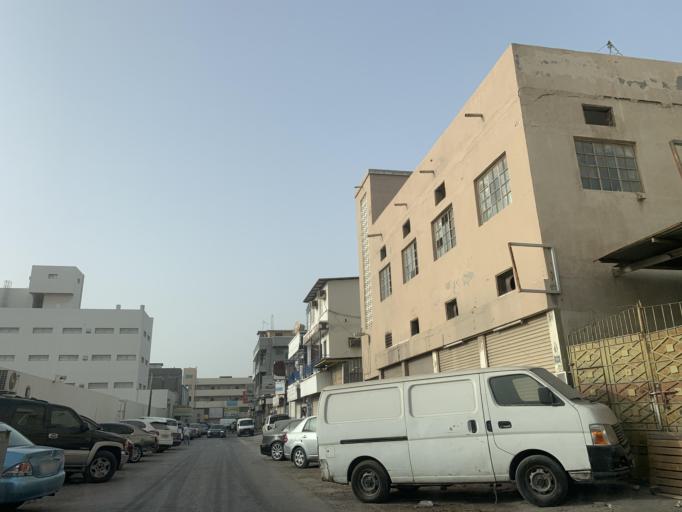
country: BH
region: Northern
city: Madinat `Isa
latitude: 26.1851
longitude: 50.5300
